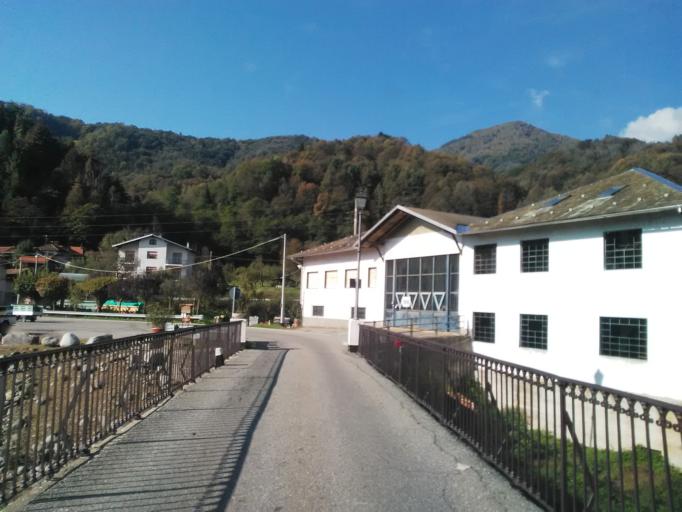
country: IT
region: Piedmont
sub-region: Provincia di Vercelli
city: Postua
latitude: 45.7117
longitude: 8.2294
